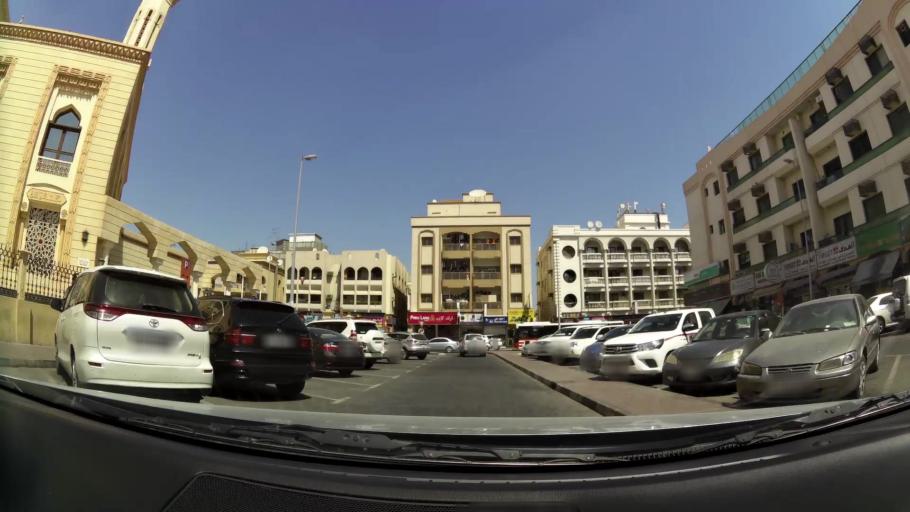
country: AE
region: Ash Shariqah
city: Sharjah
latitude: 25.2325
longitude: 55.2775
